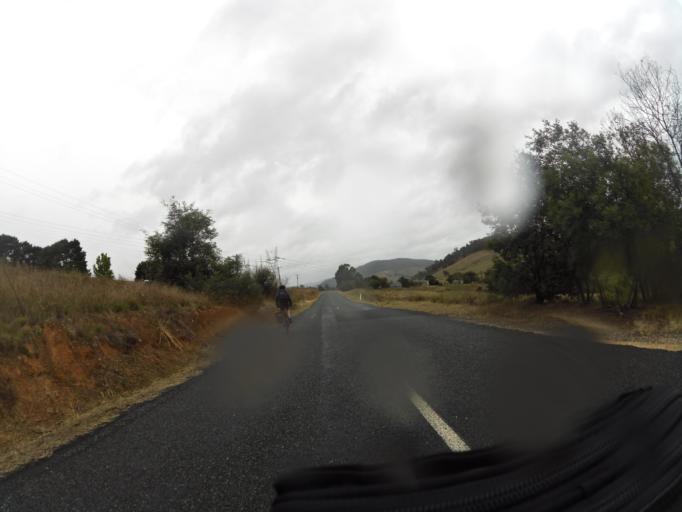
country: AU
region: New South Wales
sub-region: Greater Hume Shire
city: Holbrook
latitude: -36.2248
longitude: 147.6605
